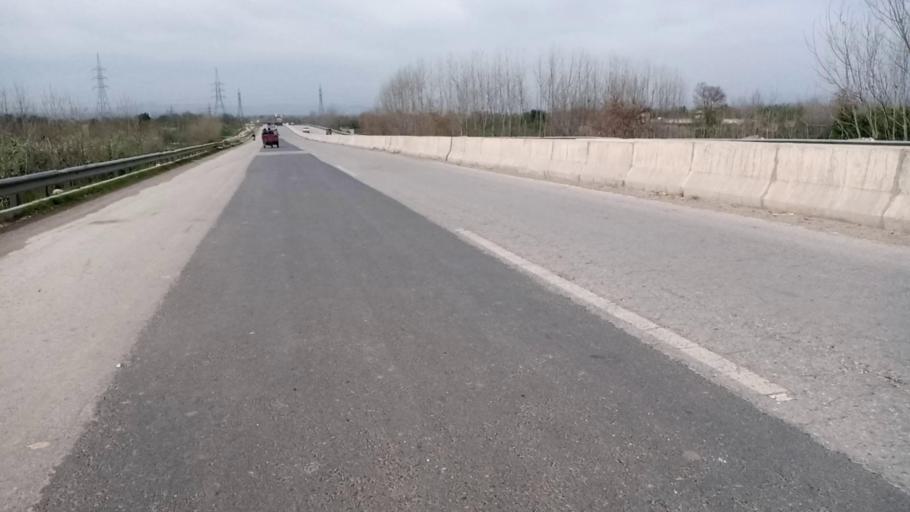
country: PK
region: Khyber Pakhtunkhwa
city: Peshawar
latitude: 34.0606
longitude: 71.6067
